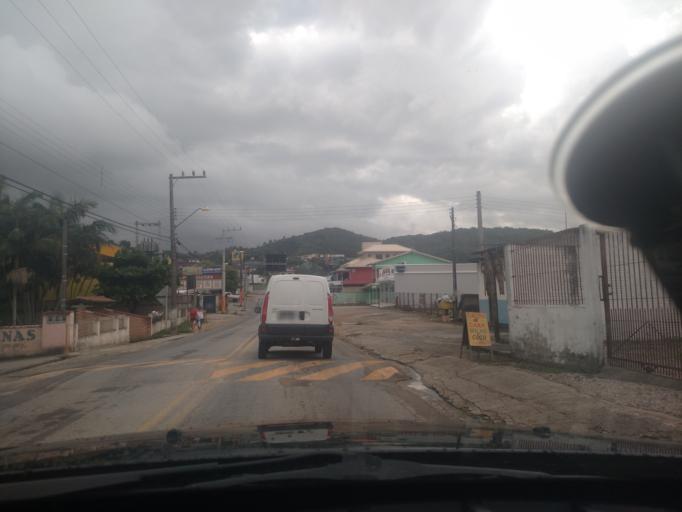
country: BR
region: Santa Catarina
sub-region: Biguacu
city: Biguacu
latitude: -27.3778
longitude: -48.6290
